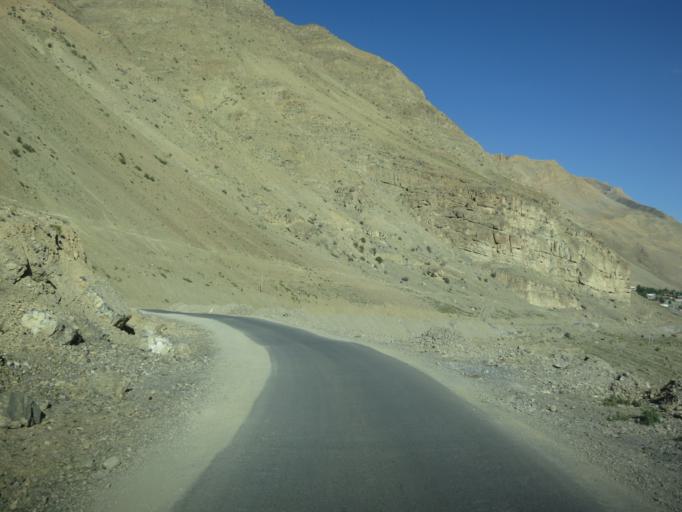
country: IN
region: Himachal Pradesh
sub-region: Shimla
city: Sarahan
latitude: 32.2355
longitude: 78.0619
